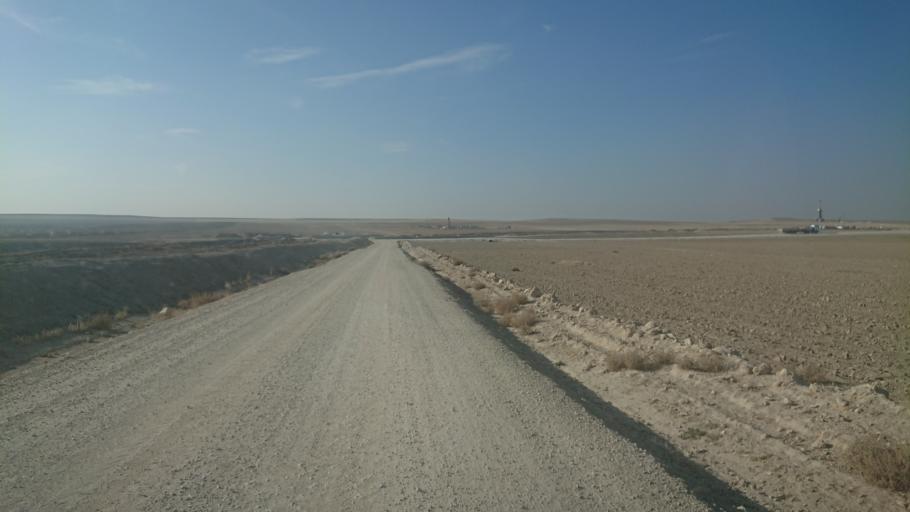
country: TR
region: Aksaray
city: Sultanhani
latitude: 38.0678
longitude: 33.6188
